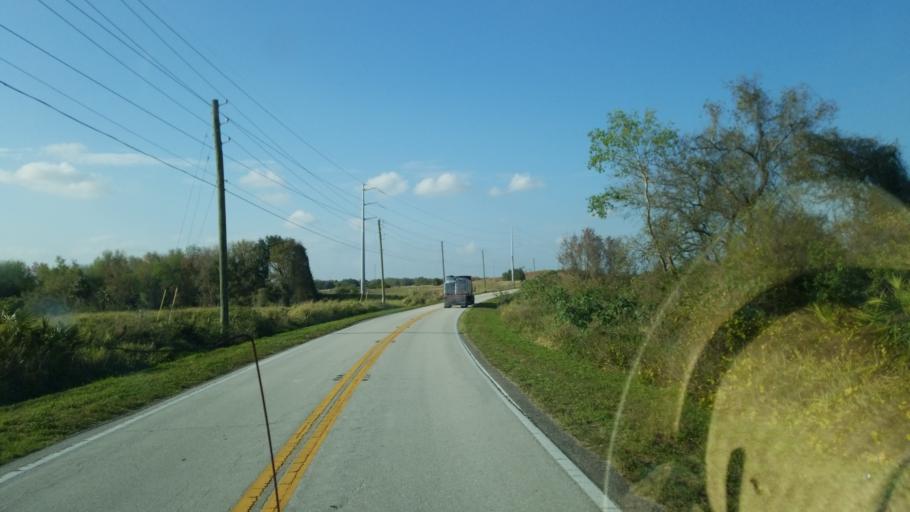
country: US
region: Florida
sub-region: Polk County
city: Mulberry
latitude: 27.7326
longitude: -81.9727
